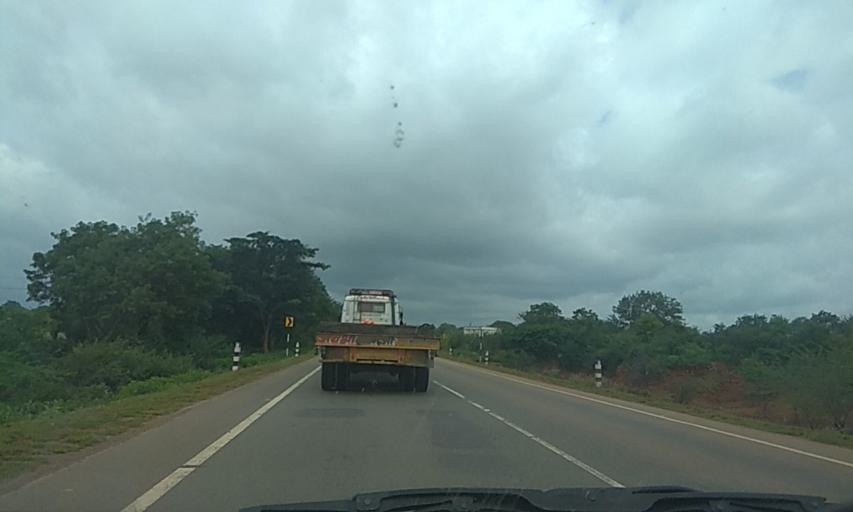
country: IN
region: Karnataka
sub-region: Dharwad
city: Hubli
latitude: 15.3341
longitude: 75.0964
